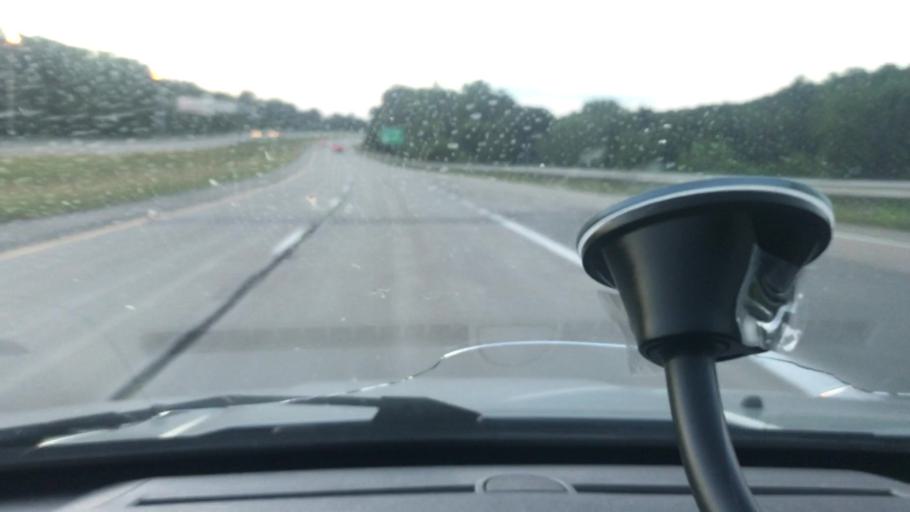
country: US
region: Illinois
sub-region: Peoria County
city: Bellevue
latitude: 40.7472
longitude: -89.6683
